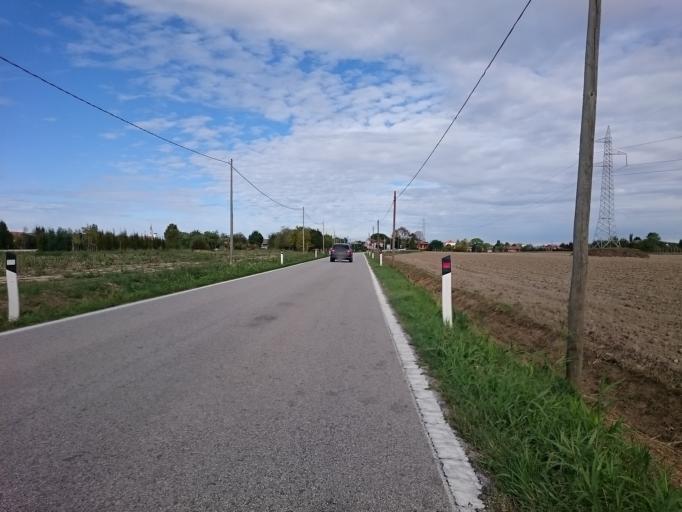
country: IT
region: Veneto
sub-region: Provincia di Padova
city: Bovolenta
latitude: 45.2609
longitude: 11.9389
